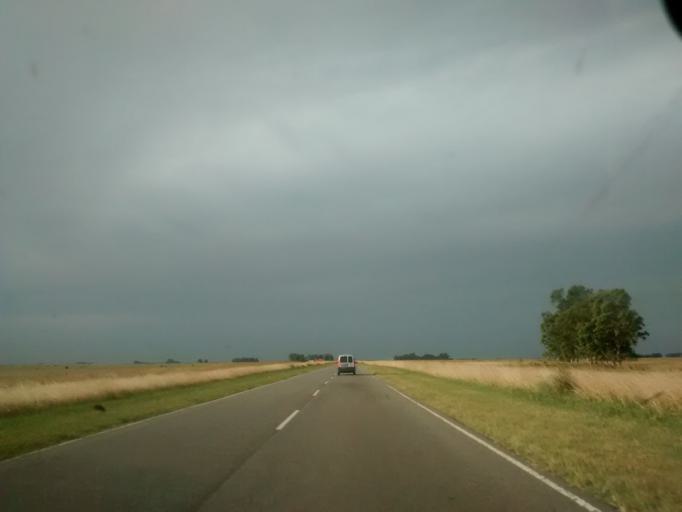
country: AR
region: Buenos Aires
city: Pila
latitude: -36.3461
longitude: -58.5813
